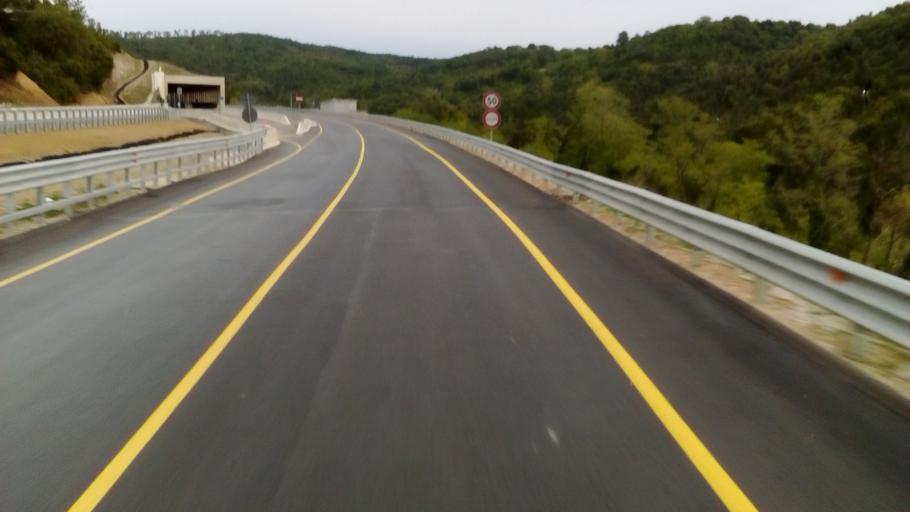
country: IT
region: Tuscany
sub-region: Provincia di Grosseto
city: Civitella Marittima
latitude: 43.0444
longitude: 11.2859
